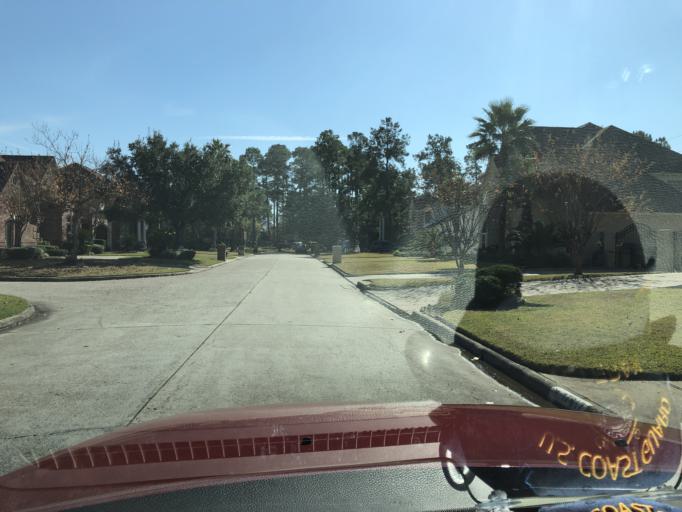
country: US
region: Texas
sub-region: Harris County
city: Tomball
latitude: 30.0200
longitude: -95.5492
